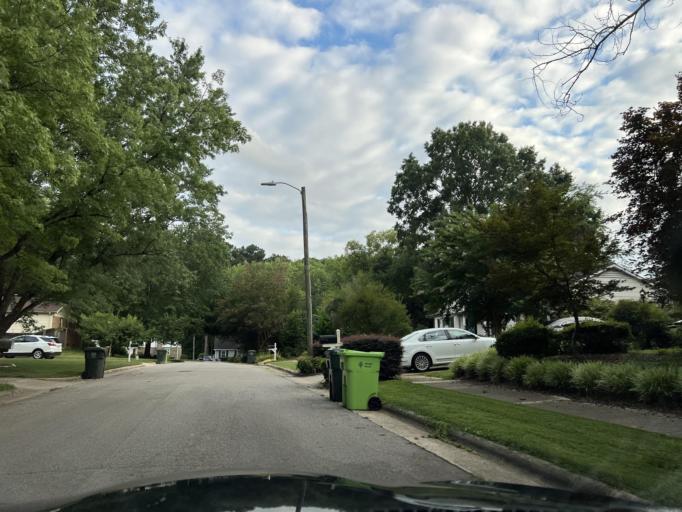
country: US
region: North Carolina
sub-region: Wake County
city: West Raleigh
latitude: 35.8609
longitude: -78.6526
